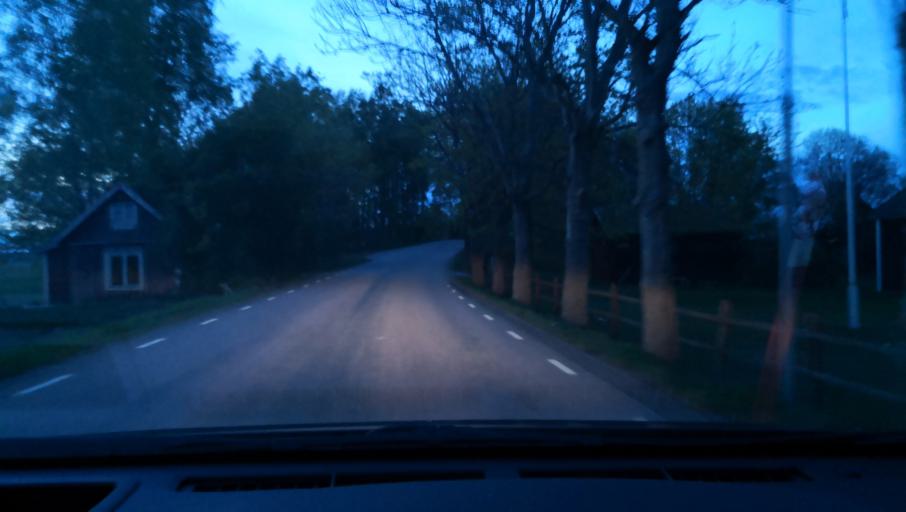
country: SE
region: OErebro
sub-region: Askersunds Kommun
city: Asbro
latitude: 59.0893
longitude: 15.0059
